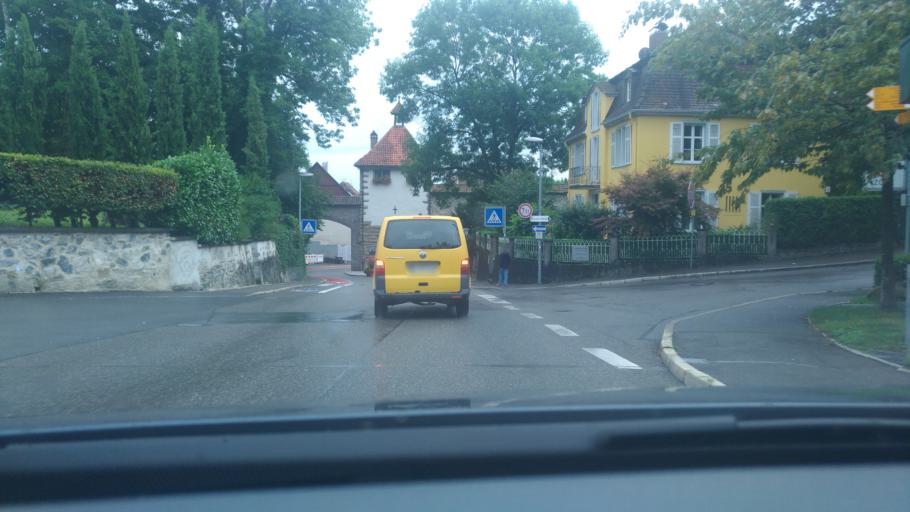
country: DE
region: Baden-Wuerttemberg
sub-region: Tuebingen Region
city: Uberlingen
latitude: 47.7712
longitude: 9.1567
